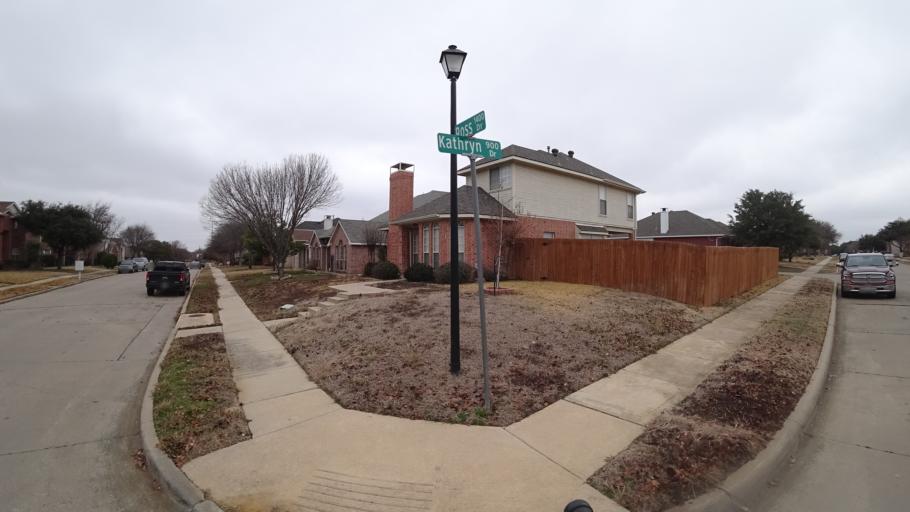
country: US
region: Texas
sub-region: Denton County
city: Lewisville
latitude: 33.0344
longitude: -97.0323
